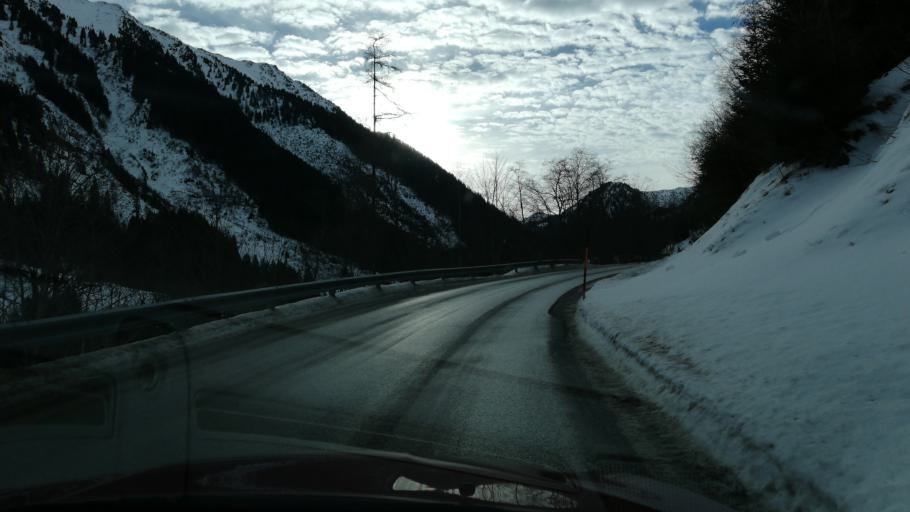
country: AT
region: Styria
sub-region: Politischer Bezirk Liezen
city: Donnersbach
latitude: 47.4314
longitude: 14.1593
